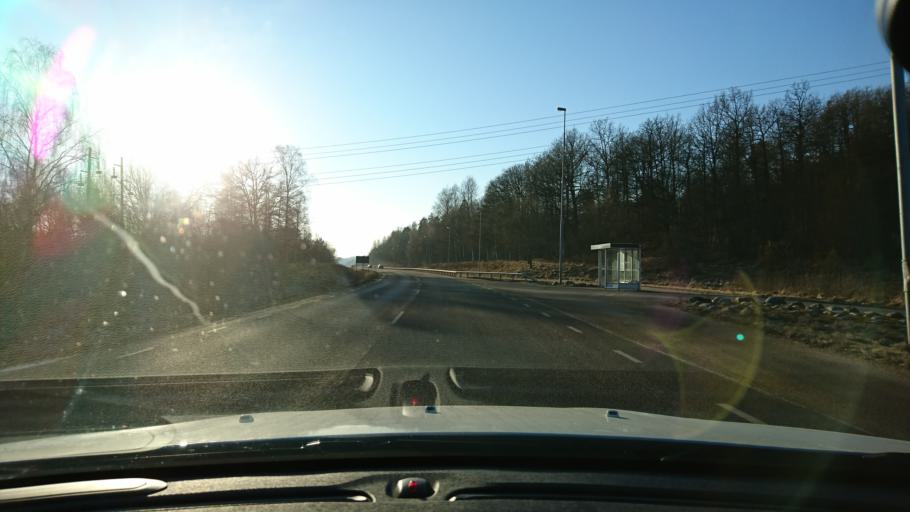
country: SE
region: Vaestra Goetaland
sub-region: Uddevalla Kommun
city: Uddevalla
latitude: 58.3577
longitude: 11.8841
